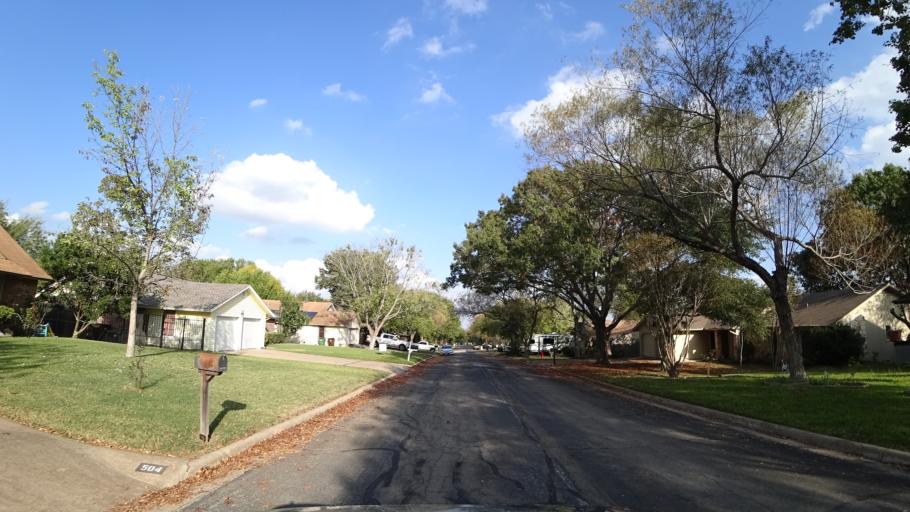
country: US
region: Texas
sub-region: Williamson County
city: Round Rock
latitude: 30.4928
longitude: -97.6706
